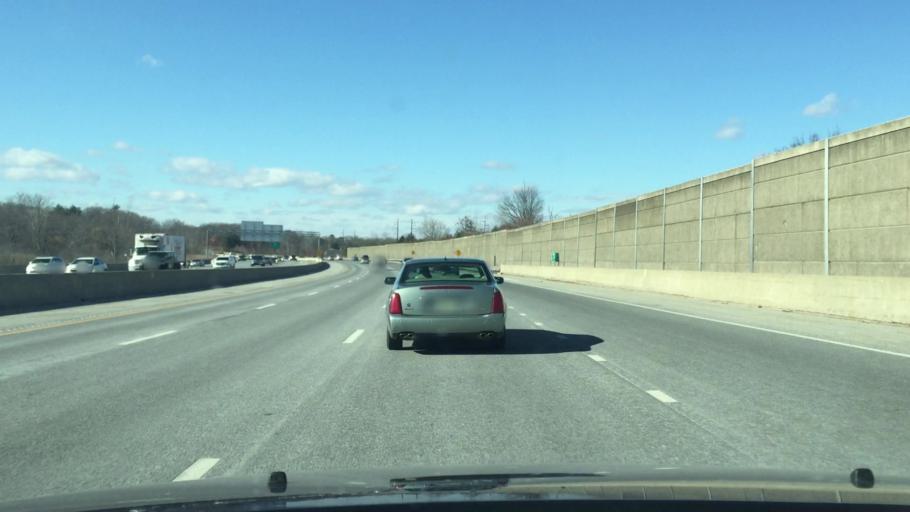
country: US
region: Massachusetts
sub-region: Middlesex County
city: Lowell
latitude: 42.6186
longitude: -71.3348
